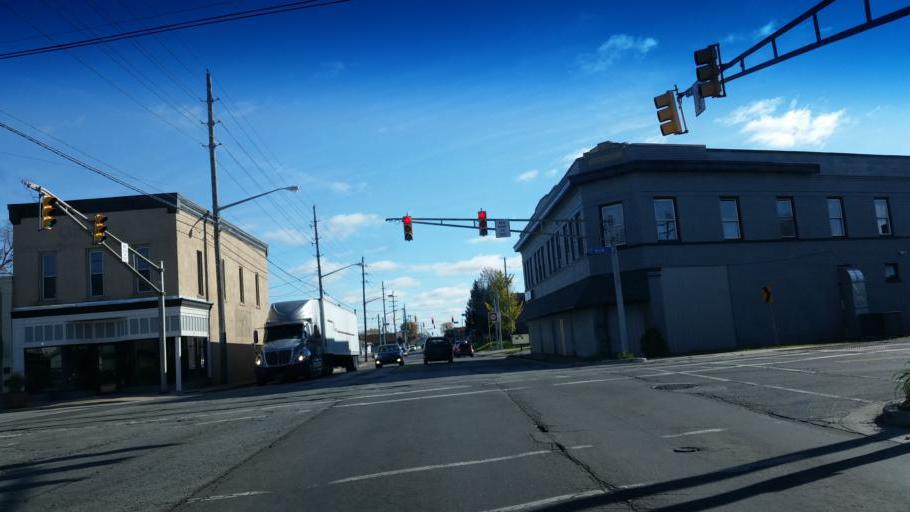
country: US
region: Indiana
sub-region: Howard County
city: Kokomo
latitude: 40.4765
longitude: -86.1313
